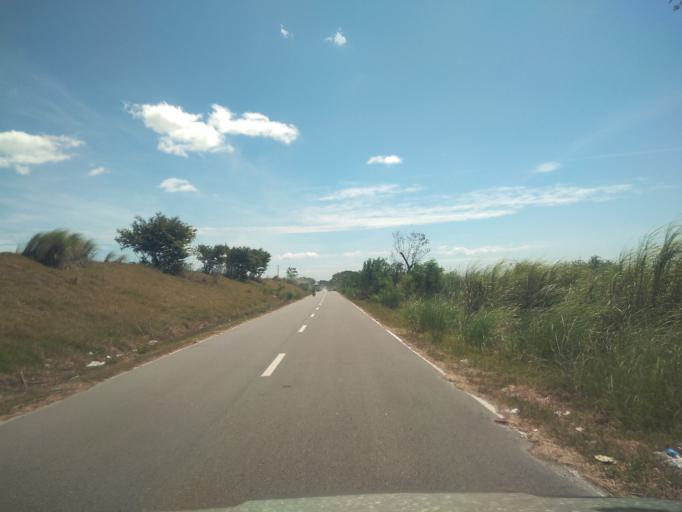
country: PH
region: Central Luzon
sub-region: Province of Pampanga
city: San Basilio
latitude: 15.0217
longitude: 120.6017
